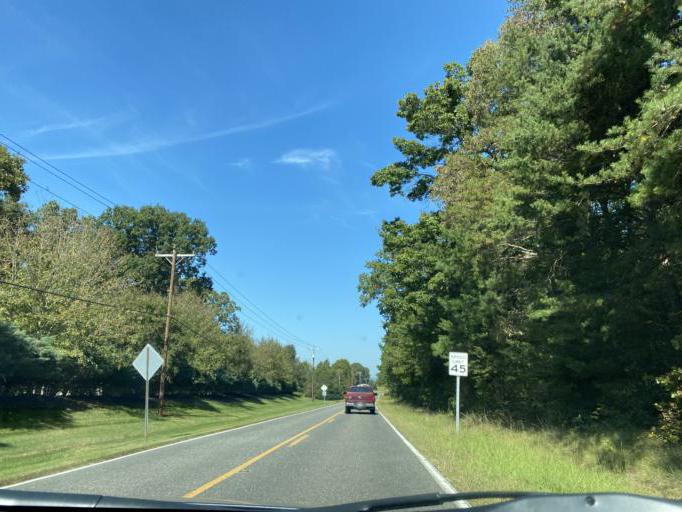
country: US
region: North Carolina
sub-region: Cleveland County
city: Boiling Springs
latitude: 35.2800
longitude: -81.6661
